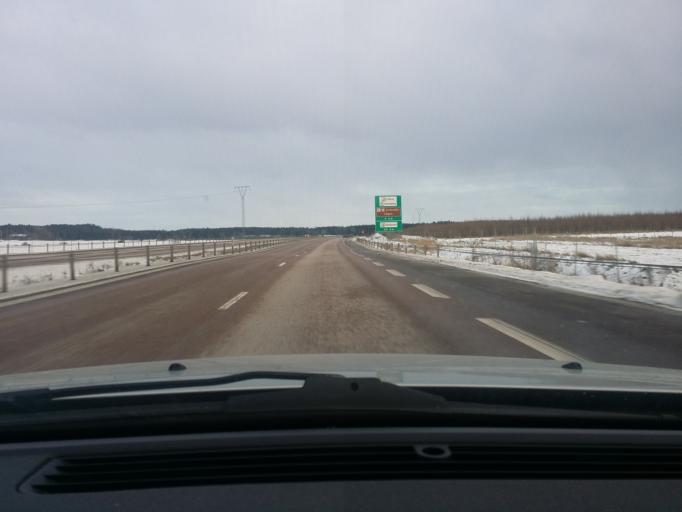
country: SE
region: Uppsala
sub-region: Enkopings Kommun
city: Hummelsta
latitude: 59.6314
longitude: 16.8457
